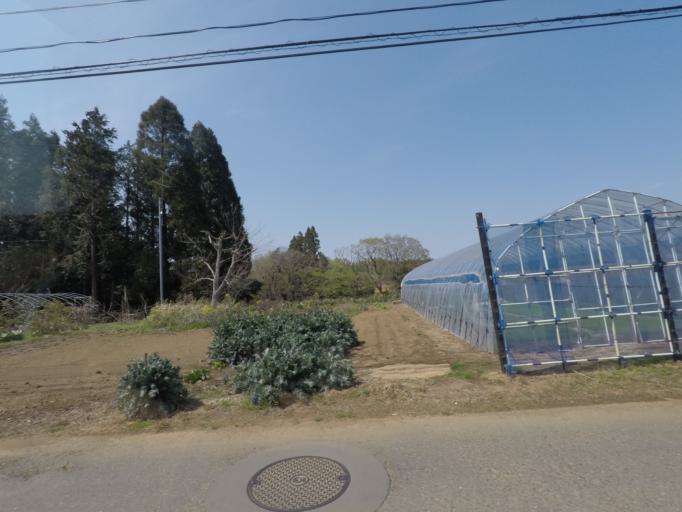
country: JP
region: Chiba
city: Naruto
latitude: 35.7043
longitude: 140.4097
